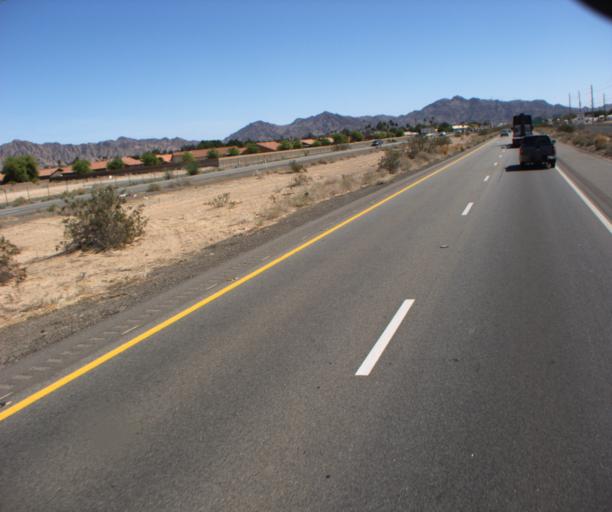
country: US
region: Arizona
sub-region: Yuma County
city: Fortuna Foothills
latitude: 32.6704
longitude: -114.4355
